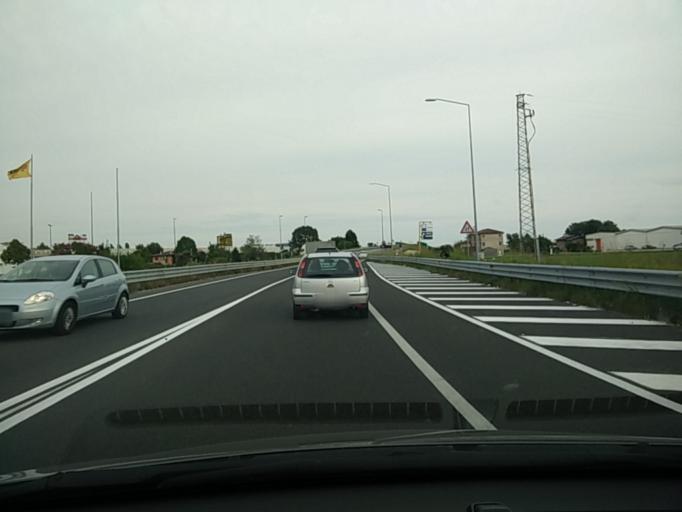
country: IT
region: Veneto
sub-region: Provincia di Venezia
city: Meolo
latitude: 45.6336
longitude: 12.4416
